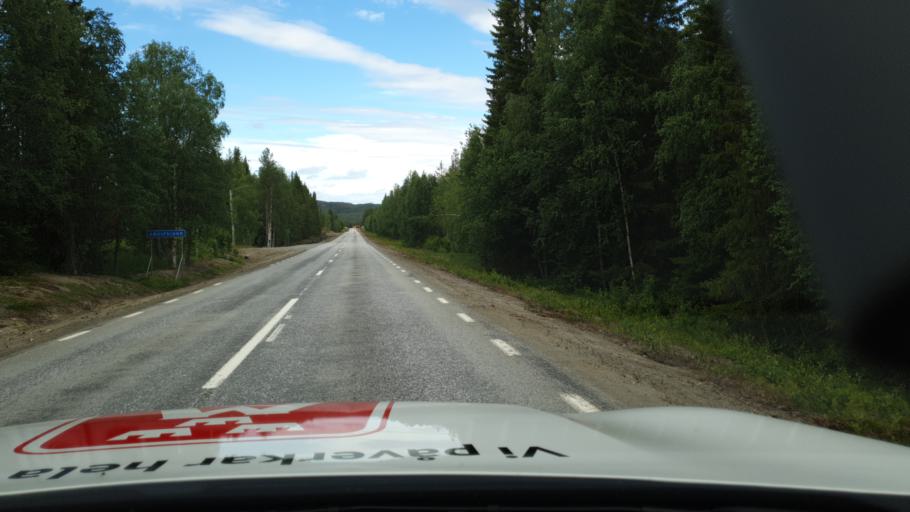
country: SE
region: Vaesterbotten
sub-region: Storumans Kommun
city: Fristad
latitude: 65.3554
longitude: 16.5647
